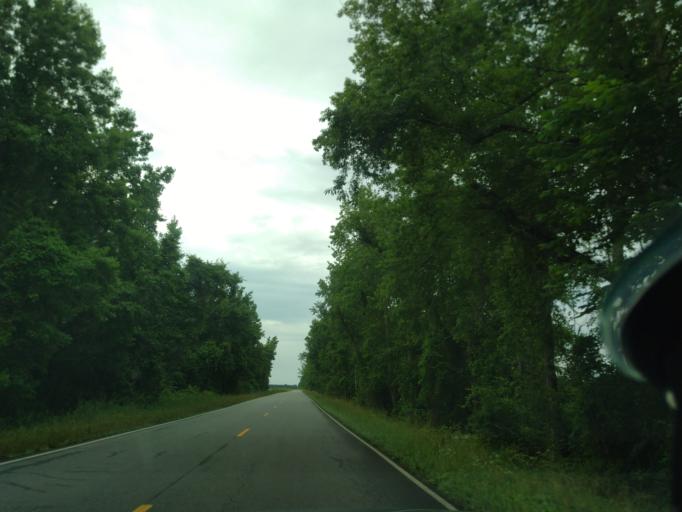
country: US
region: North Carolina
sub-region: Washington County
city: Plymouth
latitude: 35.8709
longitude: -76.5938
